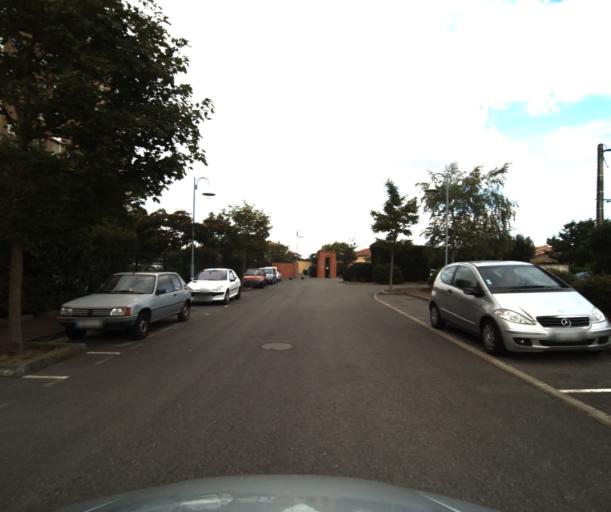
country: FR
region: Midi-Pyrenees
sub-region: Departement de la Haute-Garonne
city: Muret
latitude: 43.4646
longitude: 1.3208
